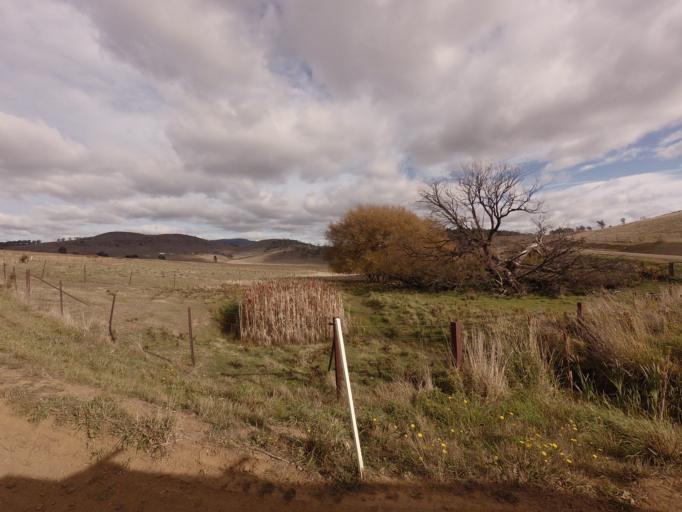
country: AU
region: Tasmania
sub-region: Brighton
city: Bridgewater
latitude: -42.4600
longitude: 147.2774
